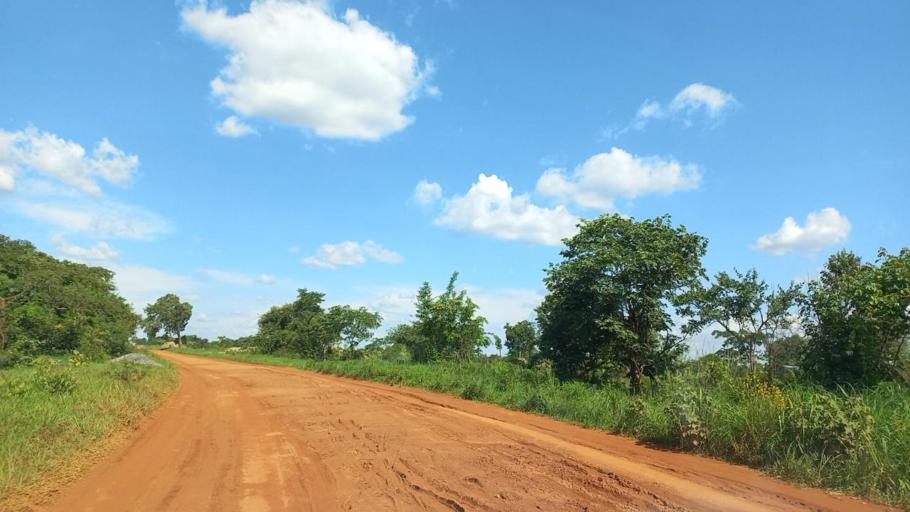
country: ZM
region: Copperbelt
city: Kitwe
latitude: -12.8699
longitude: 28.3604
